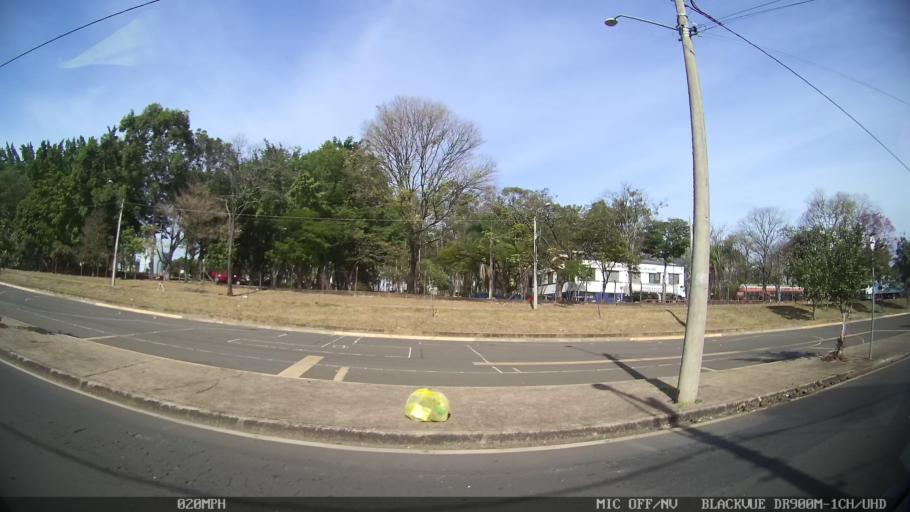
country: BR
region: Sao Paulo
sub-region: Piracicaba
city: Piracicaba
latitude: -22.7475
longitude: -47.6320
